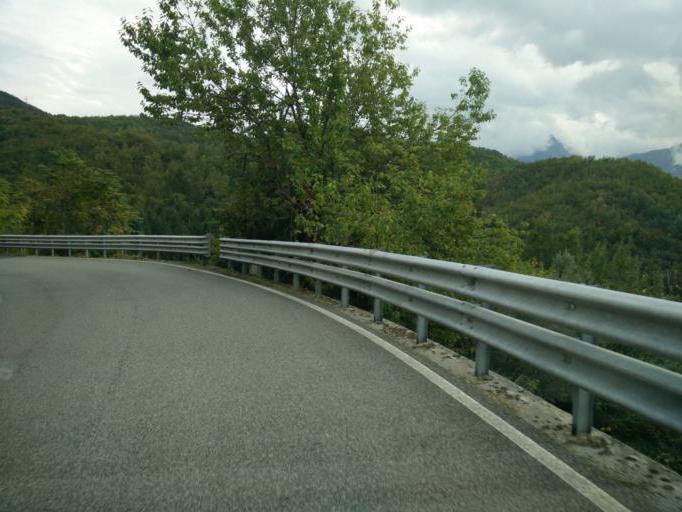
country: IT
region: Tuscany
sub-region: Provincia di Massa-Carrara
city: Casola in Lunigiana
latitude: 44.2142
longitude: 10.1890
